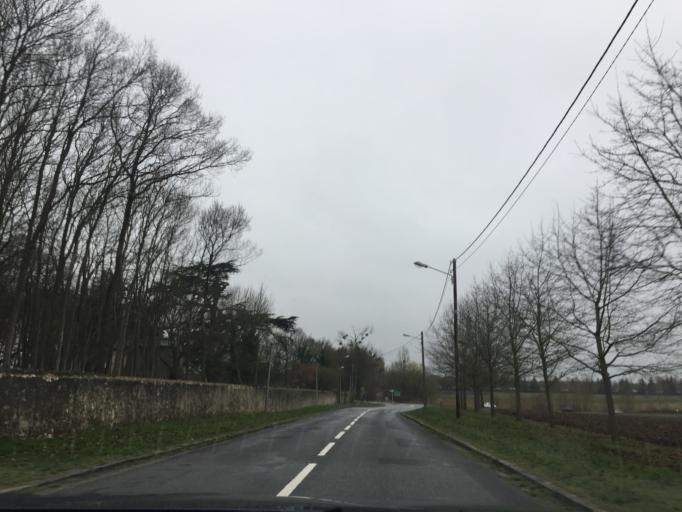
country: FR
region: Ile-de-France
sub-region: Departement de Seine-et-Marne
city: Coupvray
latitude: 48.8843
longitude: 2.7930
